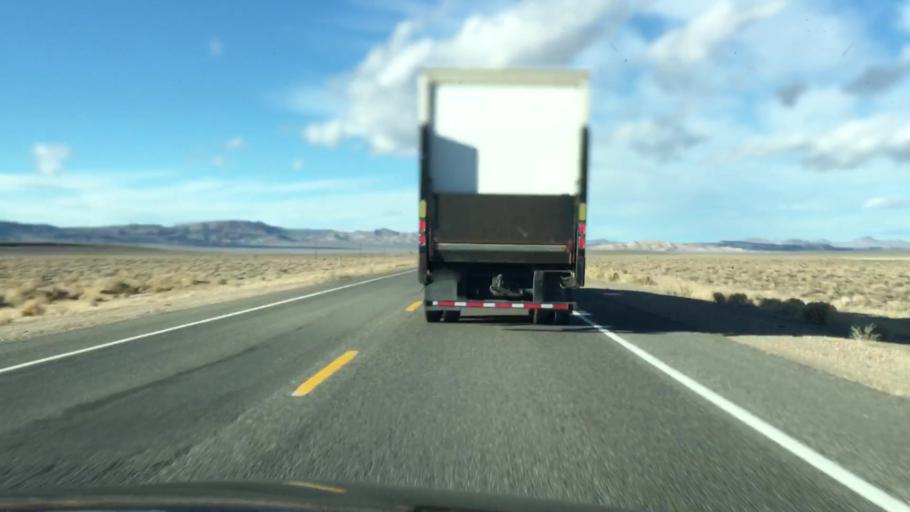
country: US
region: Nevada
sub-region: Esmeralda County
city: Goldfield
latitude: 37.4355
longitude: -117.1624
